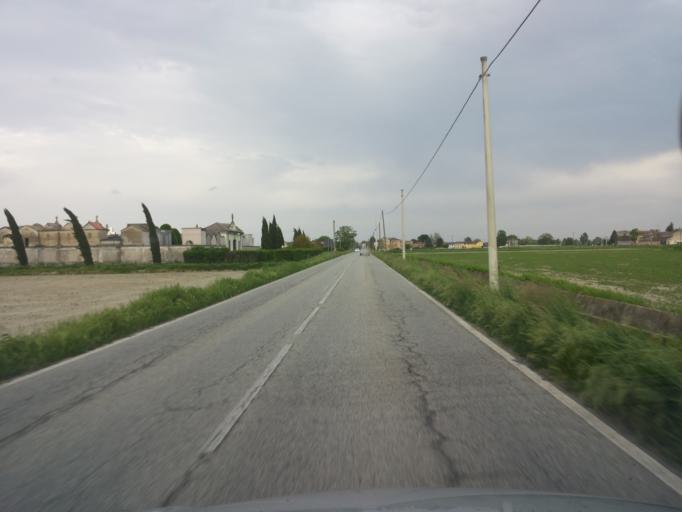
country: IT
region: Piedmont
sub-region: Provincia di Vercelli
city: Motta De Conti
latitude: 45.1633
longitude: 8.5117
